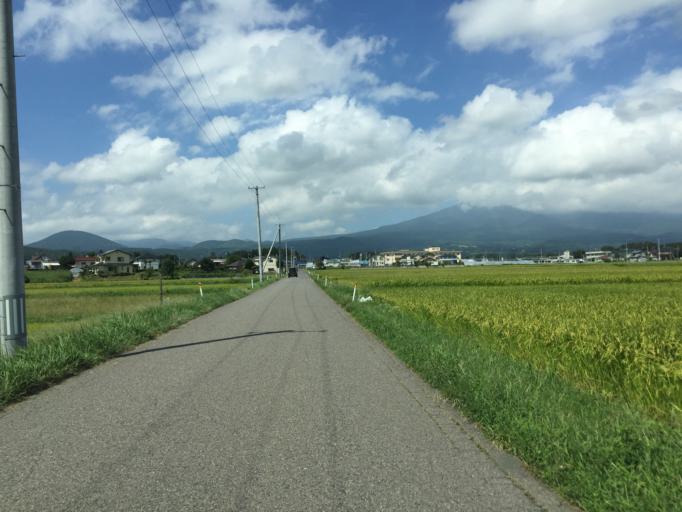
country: JP
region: Fukushima
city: Motomiya
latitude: 37.5301
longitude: 140.3745
